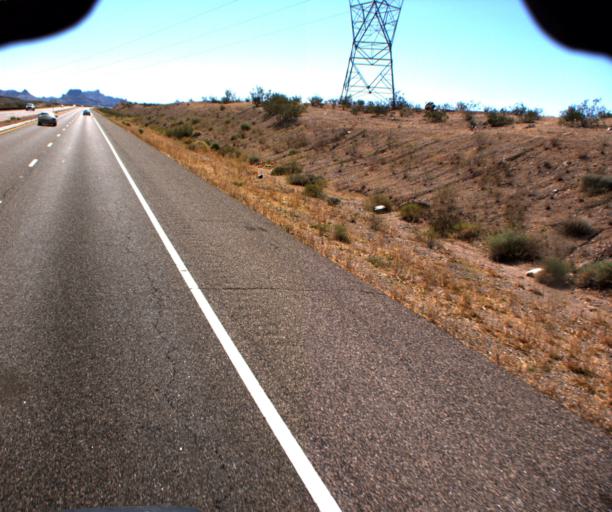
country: US
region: Nevada
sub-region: Clark County
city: Laughlin
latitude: 35.1900
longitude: -114.5143
